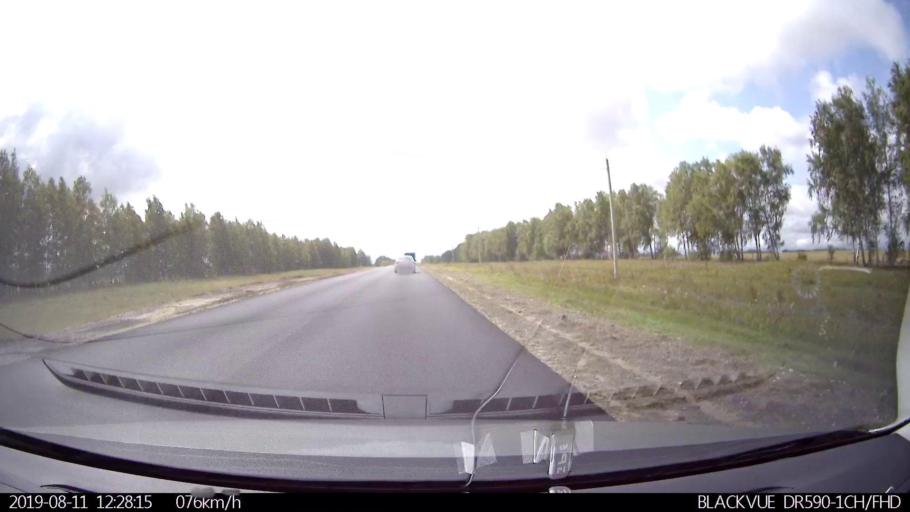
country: RU
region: Ulyanovsk
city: Ignatovka
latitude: 53.8459
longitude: 47.9134
